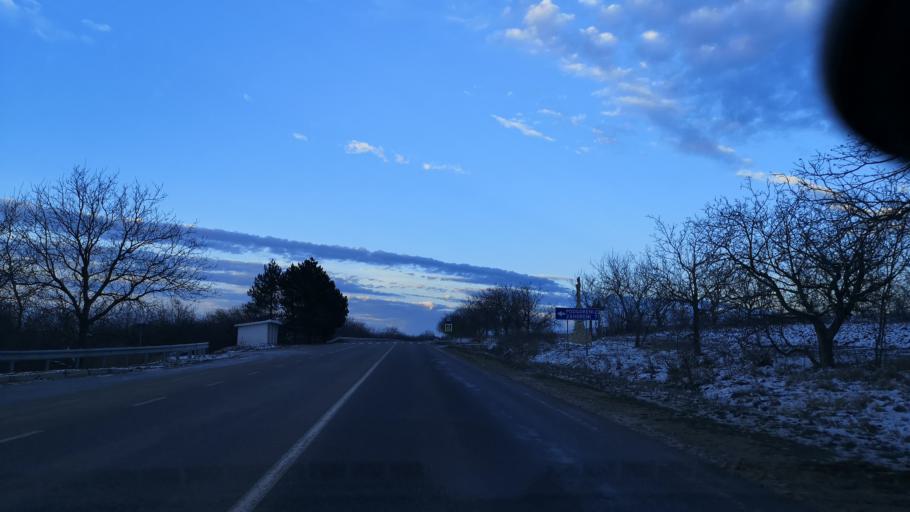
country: MD
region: Orhei
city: Orhei
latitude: 47.5514
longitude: 28.7938
